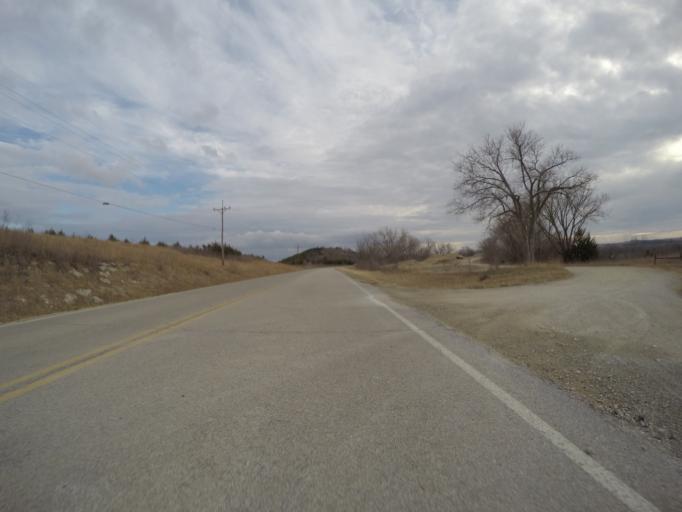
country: US
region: Kansas
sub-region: Riley County
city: Manhattan
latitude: 39.2578
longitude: -96.5694
